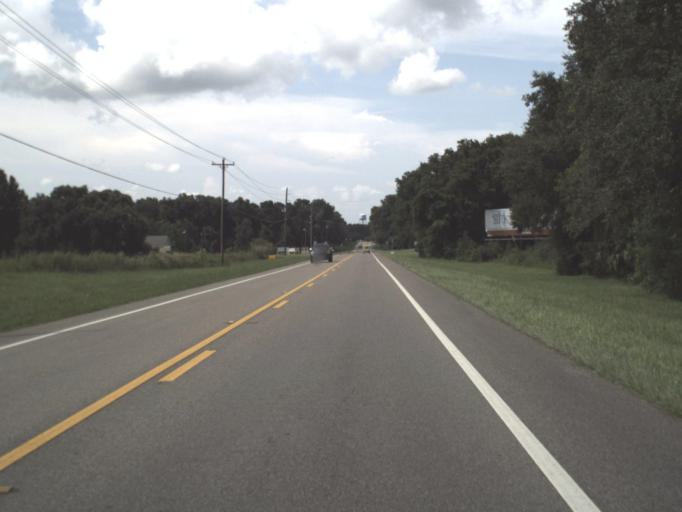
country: US
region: Florida
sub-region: Citrus County
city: Floral City
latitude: 28.7680
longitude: -82.2938
